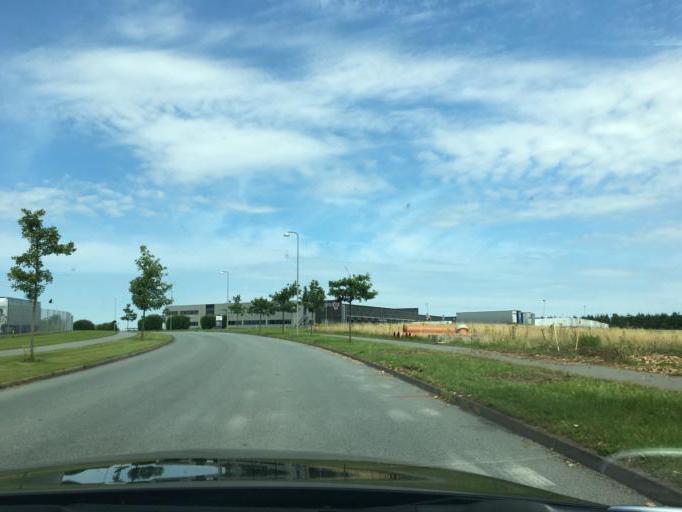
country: DK
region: South Denmark
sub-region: Kolding Kommune
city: Kolding
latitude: 55.5439
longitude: 9.4701
